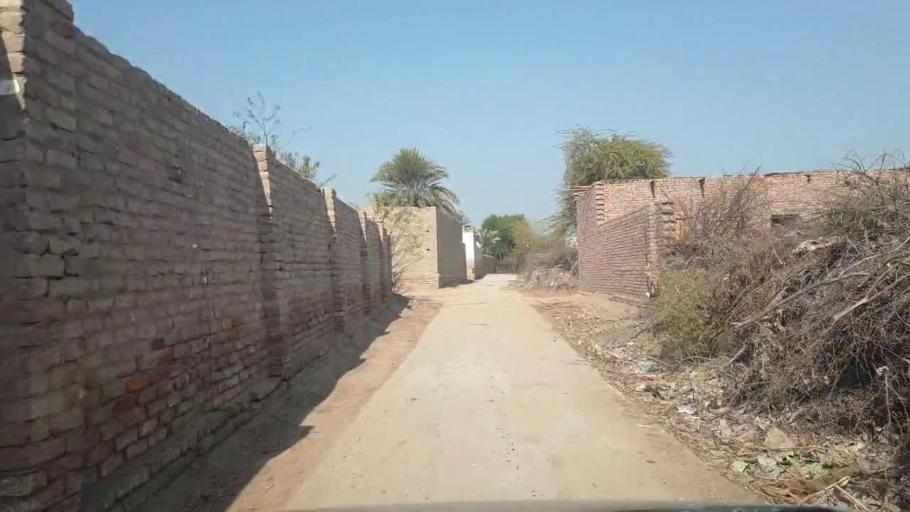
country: PK
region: Sindh
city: Tando Adam
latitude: 25.7911
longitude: 68.6318
